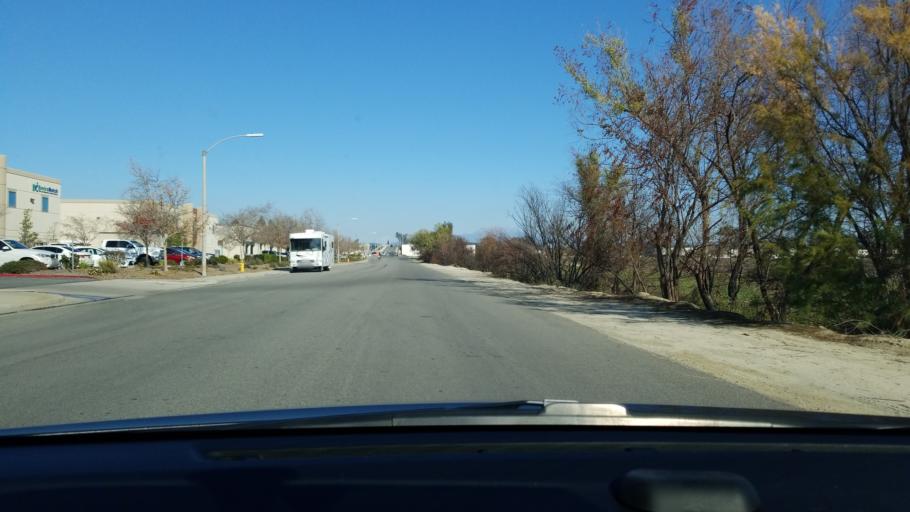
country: US
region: California
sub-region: Riverside County
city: Murrieta Hot Springs
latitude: 33.5249
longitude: -117.1750
